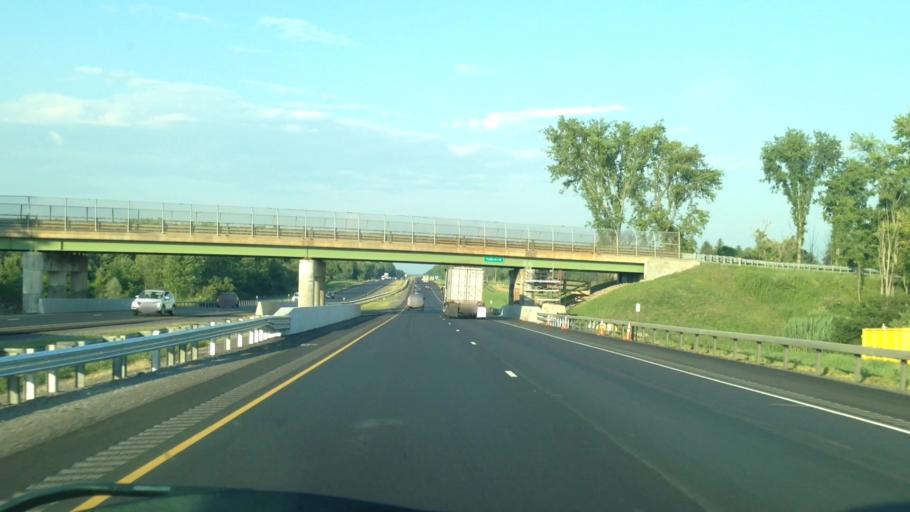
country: US
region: New York
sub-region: Oneida County
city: Vernon
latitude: 43.1280
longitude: -75.5485
